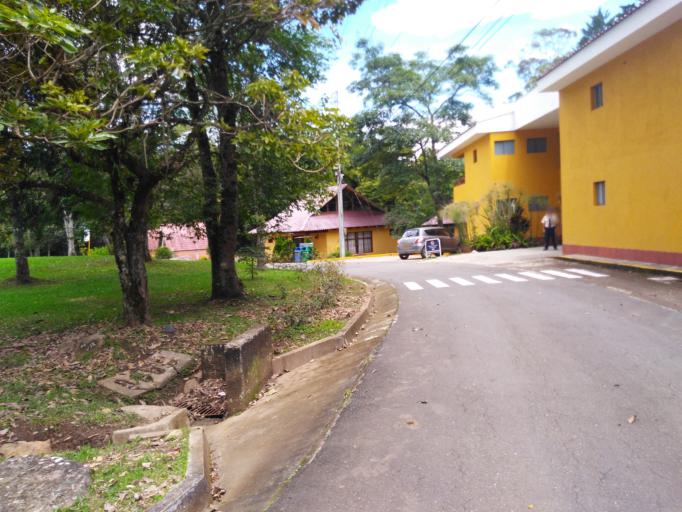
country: CO
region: Cauca
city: Popayan
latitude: 2.4778
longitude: -76.5709
